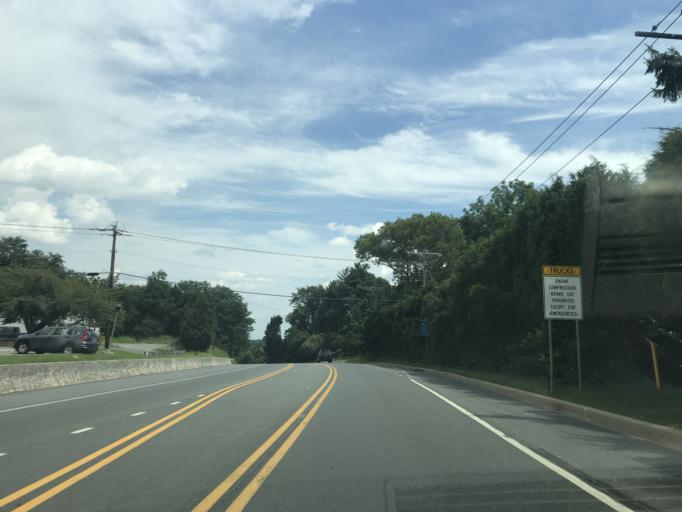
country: US
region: Delaware
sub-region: New Castle County
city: Hockessin
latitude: 39.7658
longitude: -75.6536
